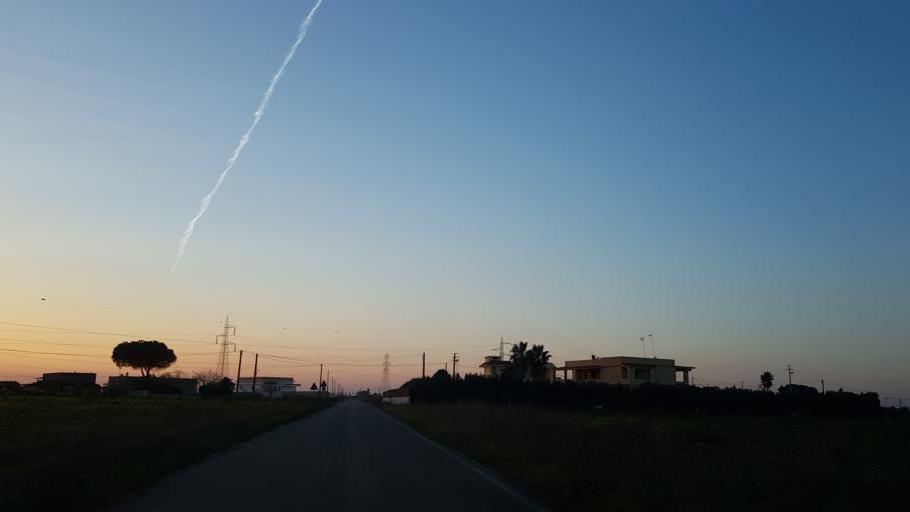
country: IT
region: Apulia
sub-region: Provincia di Brindisi
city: La Rosa
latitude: 40.5927
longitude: 17.9121
